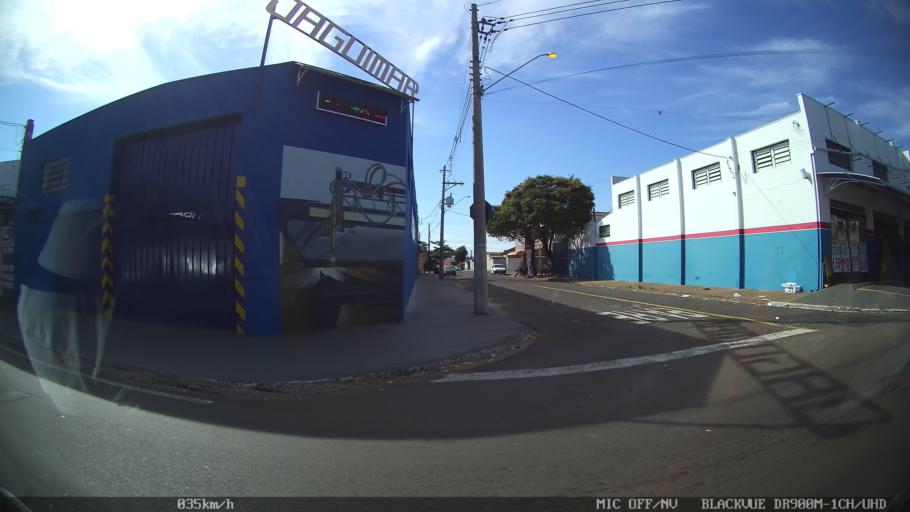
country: BR
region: Sao Paulo
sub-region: Franca
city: Franca
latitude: -20.5292
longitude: -47.4261
